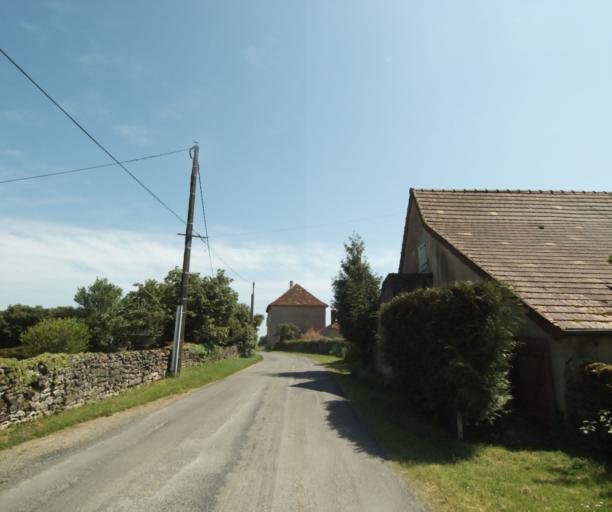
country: FR
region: Bourgogne
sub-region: Departement de Saone-et-Loire
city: Palinges
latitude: 46.5742
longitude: 4.1796
